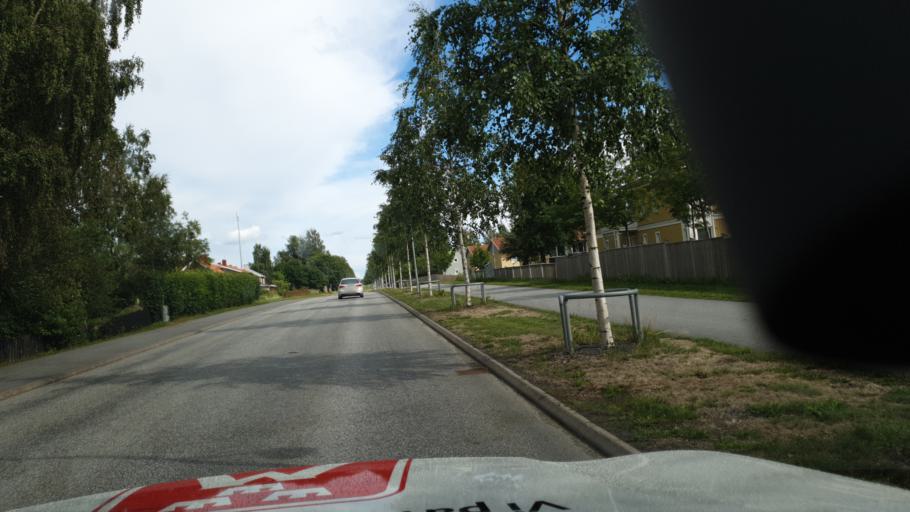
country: SE
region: Vaesterbotten
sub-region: Umea Kommun
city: Roback
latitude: 63.8360
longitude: 20.1916
